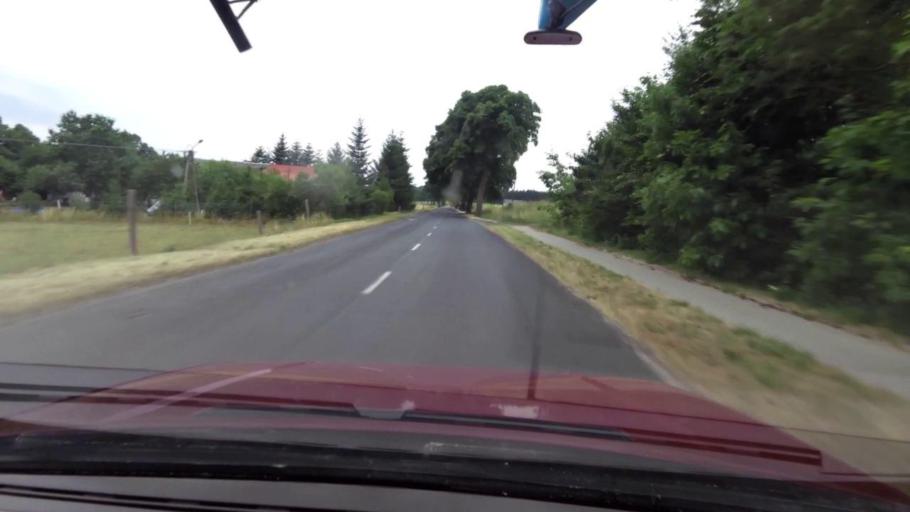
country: PL
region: West Pomeranian Voivodeship
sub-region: Powiat koszalinski
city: Sianow
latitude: 54.1655
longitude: 16.4377
